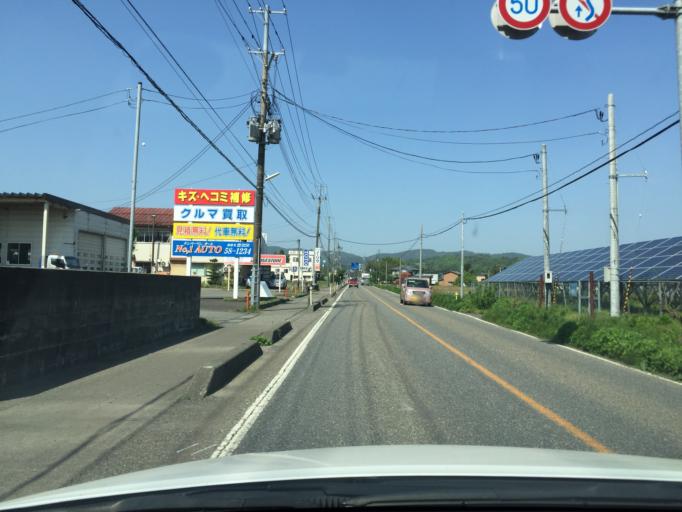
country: JP
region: Niigata
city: Muramatsu
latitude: 37.6874
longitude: 139.1544
